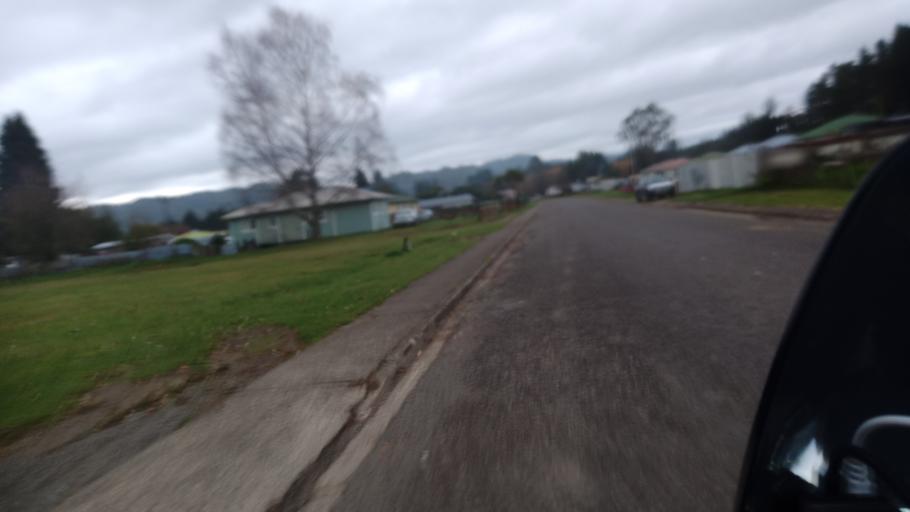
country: NZ
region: Bay of Plenty
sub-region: Whakatane District
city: Murupara
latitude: -38.6449
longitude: 176.7330
